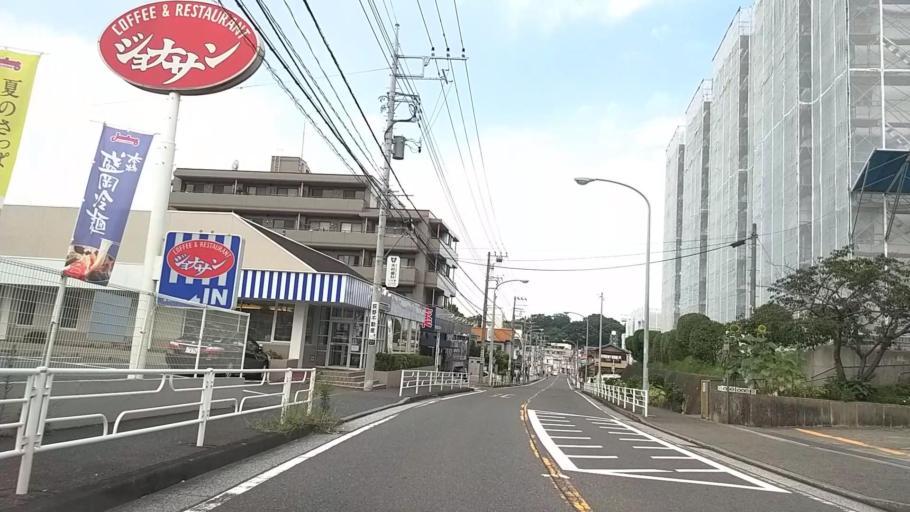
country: JP
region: Kanagawa
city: Yokohama
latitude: 35.4146
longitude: 139.5768
